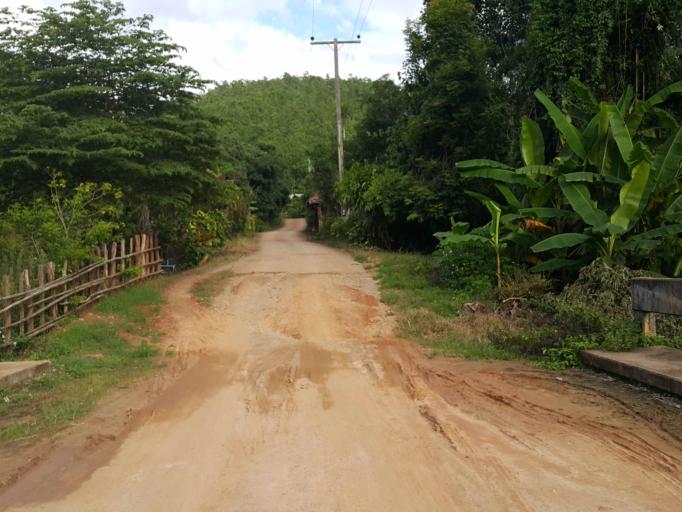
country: TH
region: Chiang Mai
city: Mae Chaem
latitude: 18.4868
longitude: 98.3857
